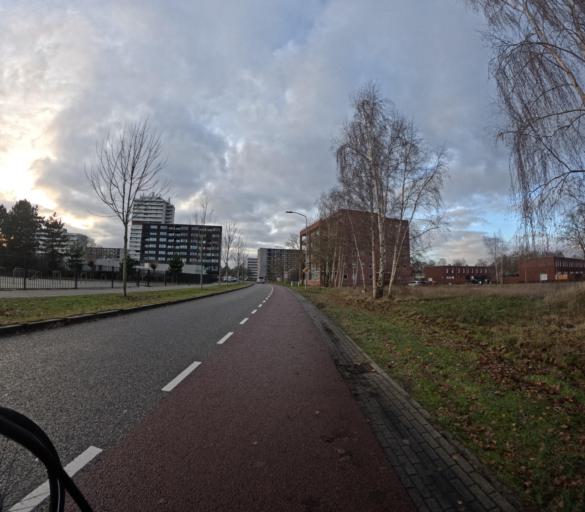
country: NL
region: Drenthe
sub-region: Gemeente Emmen
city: Emmen
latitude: 52.7931
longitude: 6.9408
